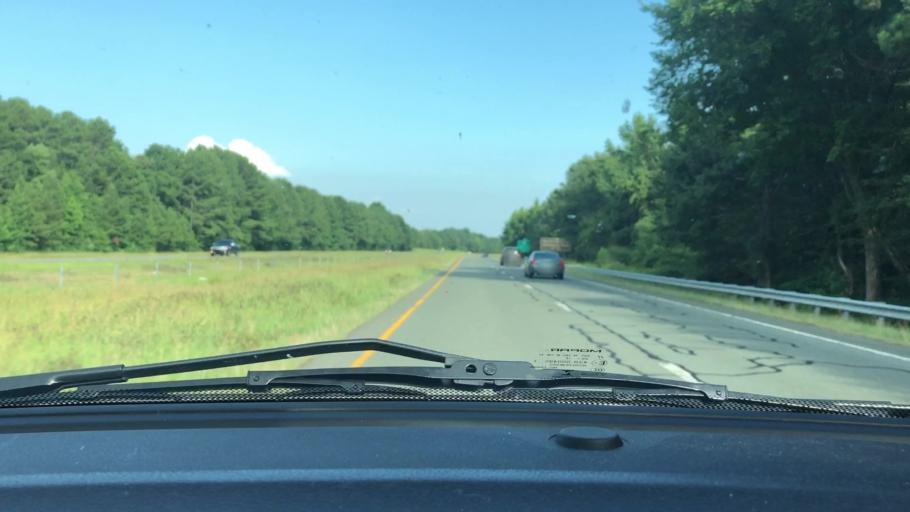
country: US
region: North Carolina
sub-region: Chatham County
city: Siler City
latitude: 35.7461
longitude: -79.4425
